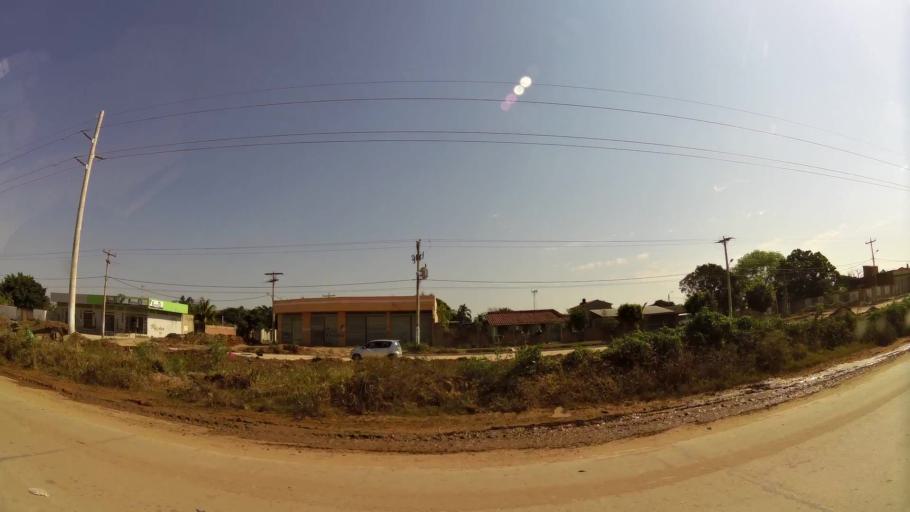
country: BO
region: Santa Cruz
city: Cotoca
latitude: -17.7471
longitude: -63.0960
